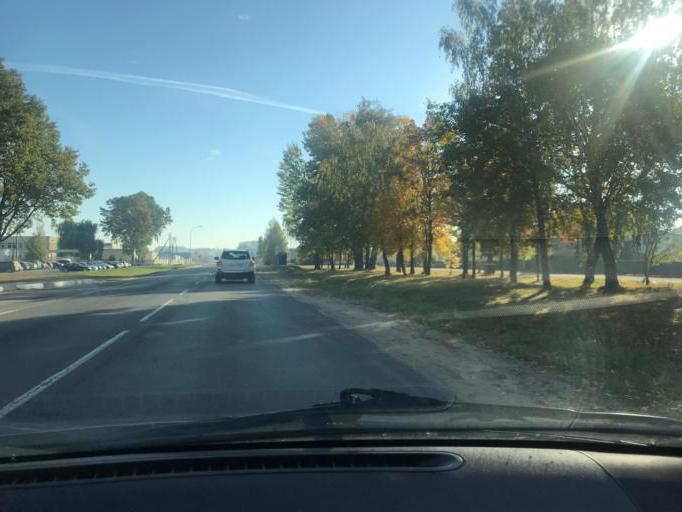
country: BY
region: Brest
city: Ivanava
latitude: 52.1434
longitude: 25.5149
